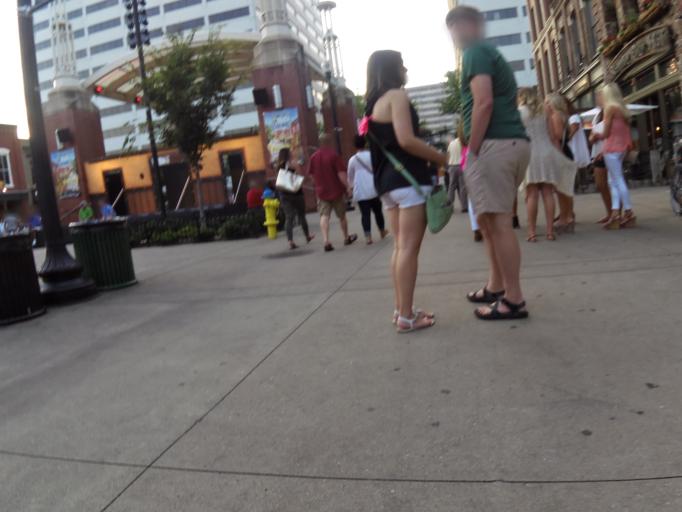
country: US
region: Tennessee
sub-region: Knox County
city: Knoxville
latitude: 35.9656
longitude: -83.9197
